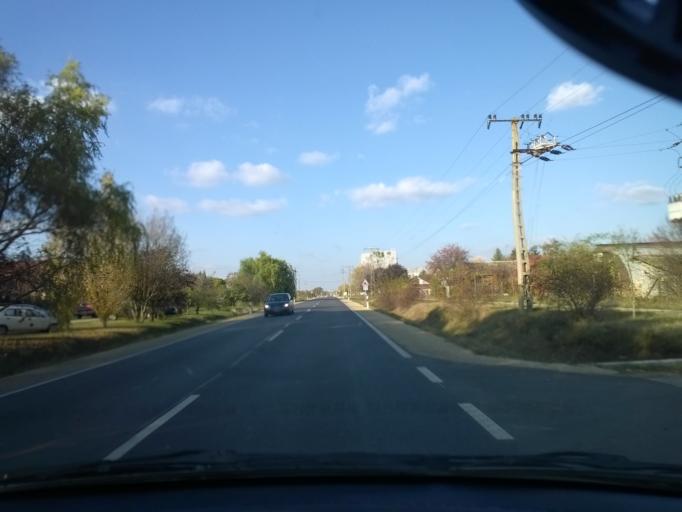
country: HU
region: Csongrad
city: Szentes
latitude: 46.6386
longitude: 20.2776
